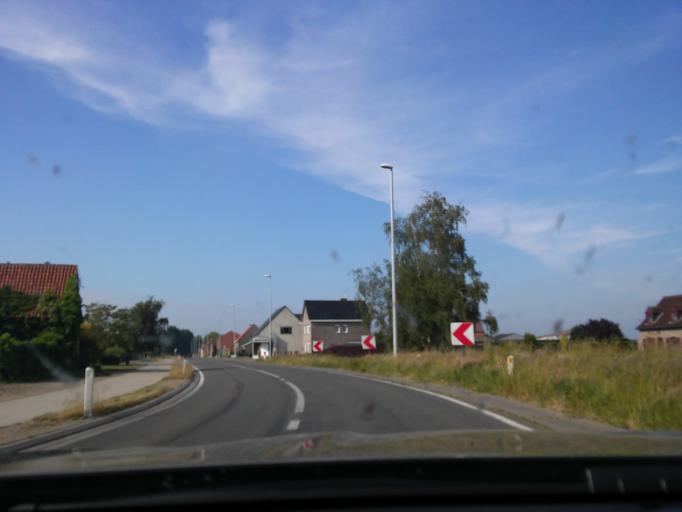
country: BE
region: Flanders
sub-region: Provincie Oost-Vlaanderen
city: Kaprijke
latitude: 51.2318
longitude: 3.5902
